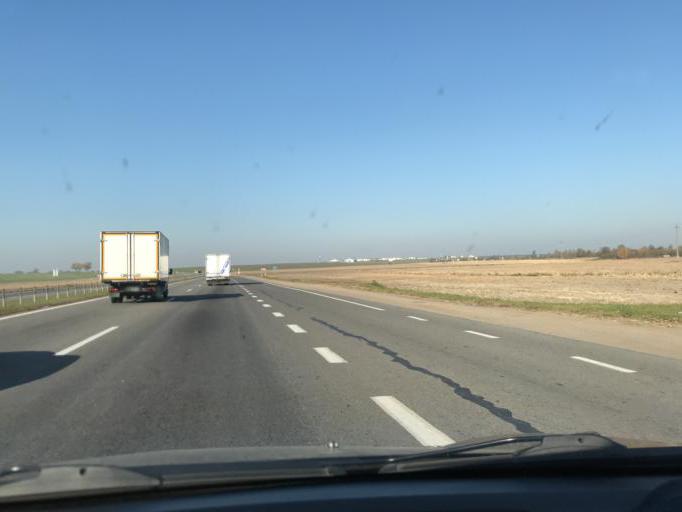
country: BY
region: Minsk
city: Dukora
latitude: 53.6703
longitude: 27.9353
